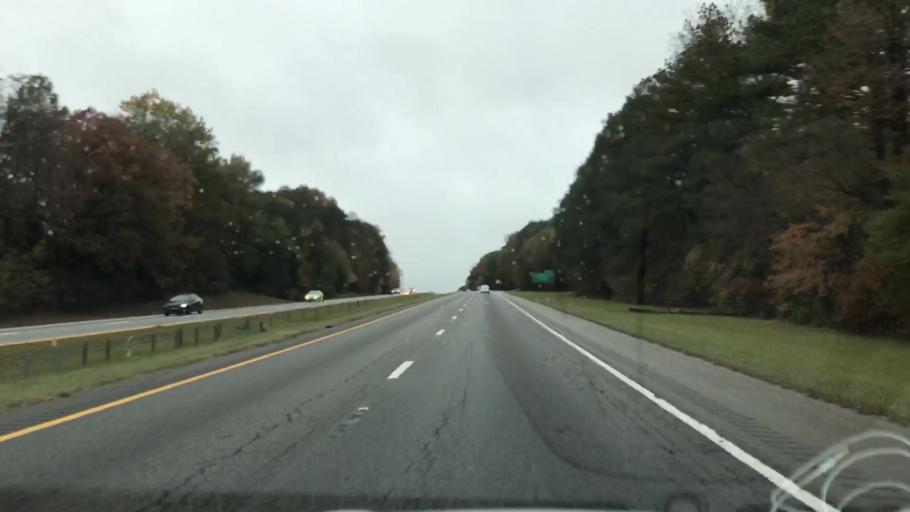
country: US
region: South Carolina
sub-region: Lexington County
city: Chapin
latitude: 34.1702
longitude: -81.3009
